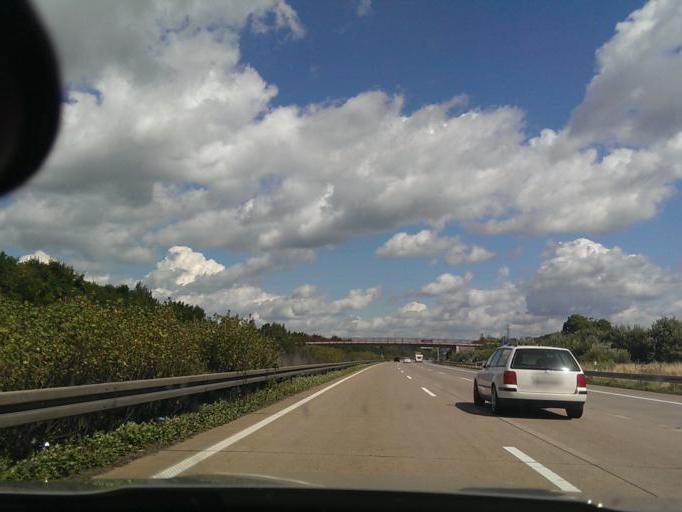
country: DE
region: Lower Saxony
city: Laatzen
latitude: 52.3253
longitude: 9.8636
